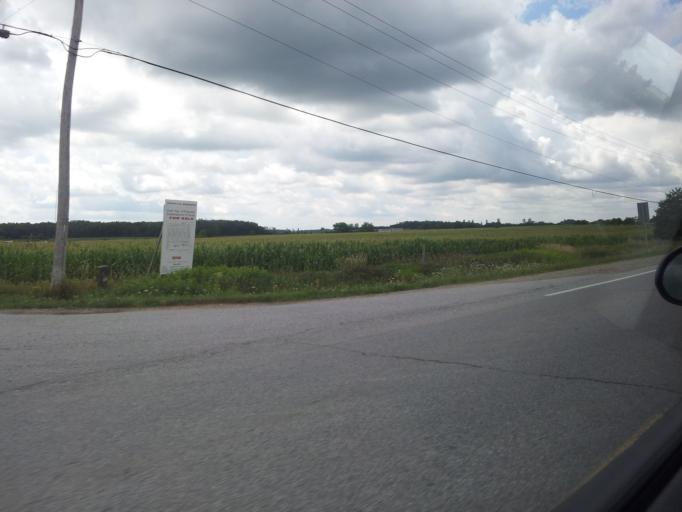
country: CA
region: Ontario
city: Stratford
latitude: 43.3697
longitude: -80.8470
